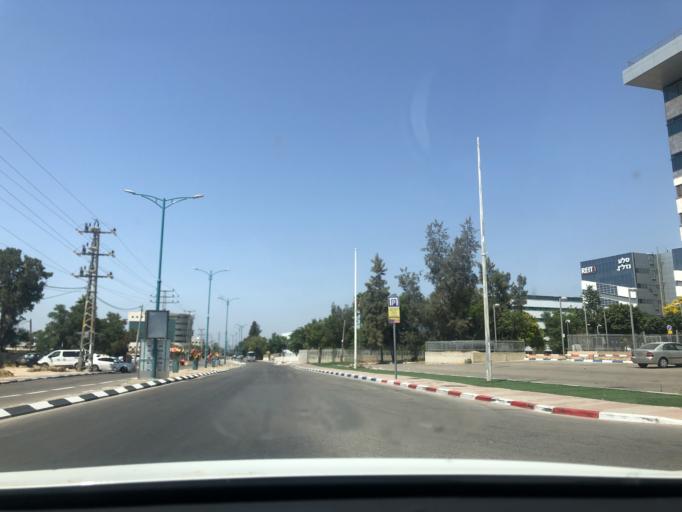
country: IL
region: Central District
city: Lod
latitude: 31.9602
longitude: 34.8988
